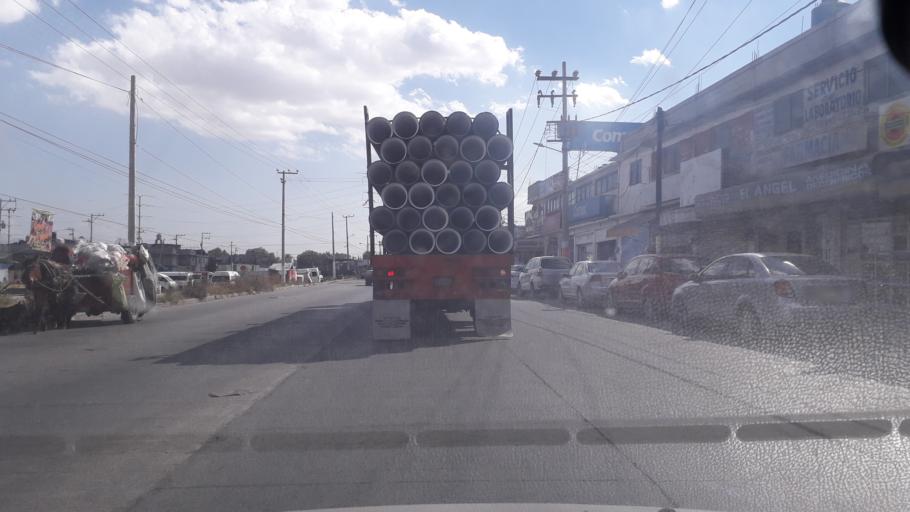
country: MX
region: Mexico
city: Ecatepec
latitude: 19.6396
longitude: -99.0578
